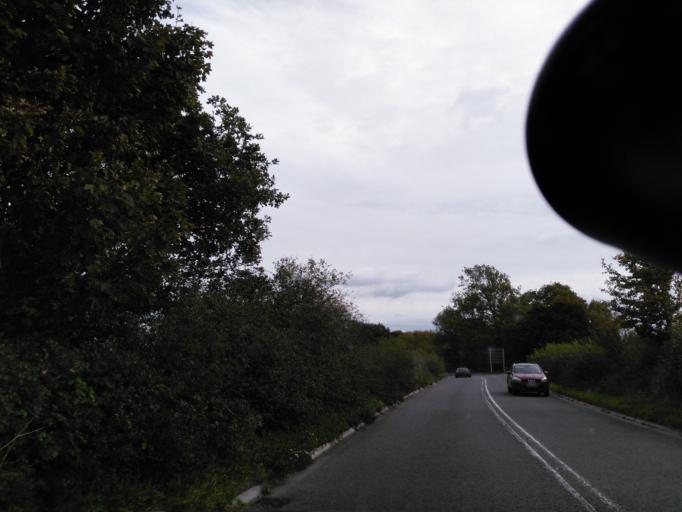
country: GB
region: England
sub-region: Wiltshire
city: Seend
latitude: 51.3518
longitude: -2.0621
